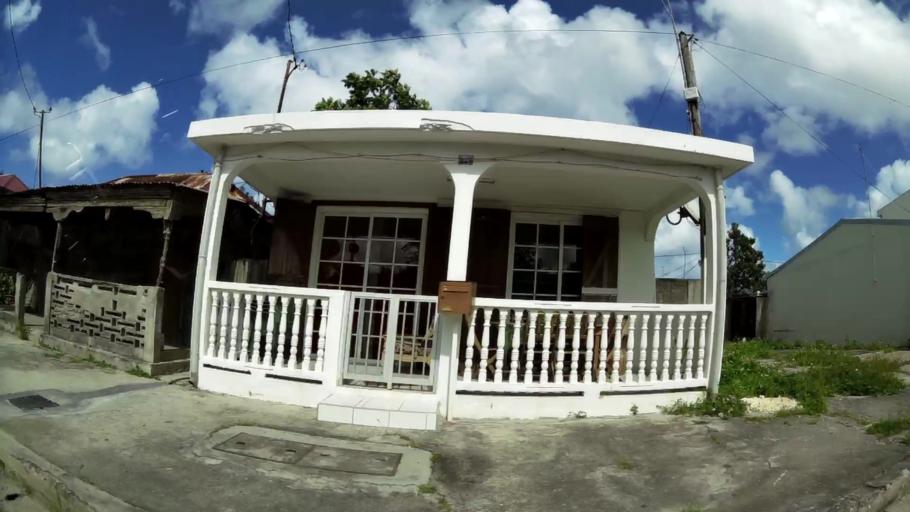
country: GP
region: Guadeloupe
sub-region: Guadeloupe
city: Port-Louis
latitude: 16.4189
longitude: -61.5301
